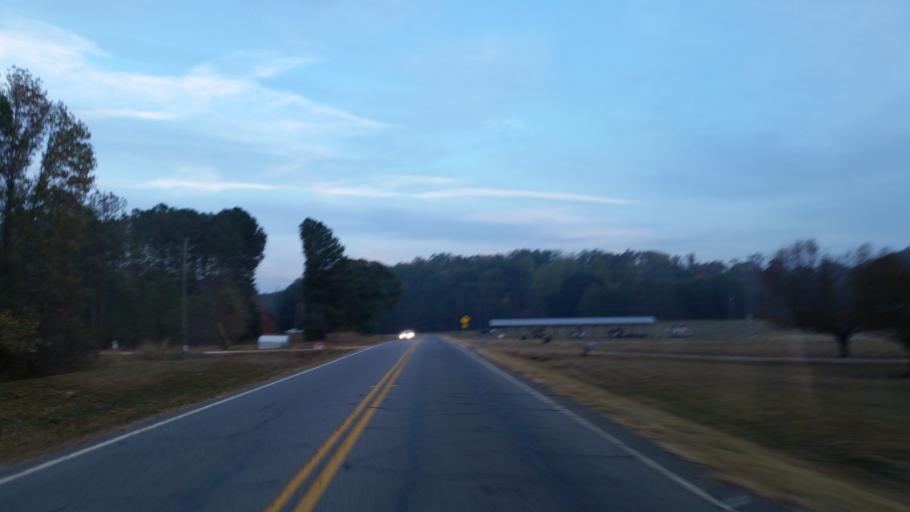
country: US
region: Georgia
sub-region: Murray County
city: Chatsworth
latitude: 34.5866
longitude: -84.7135
